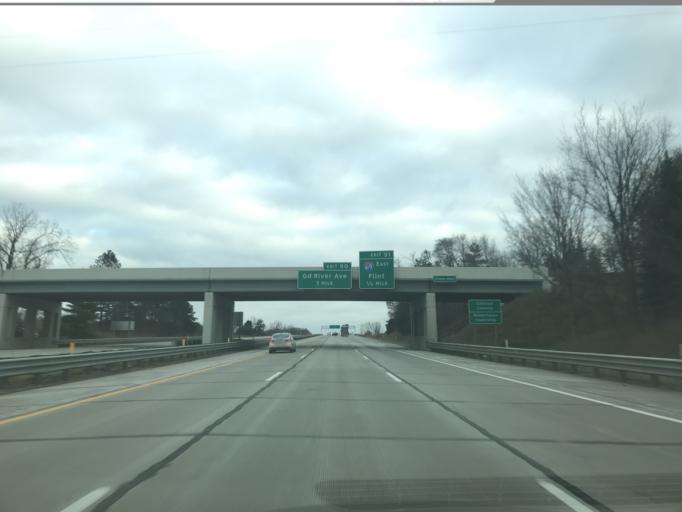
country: US
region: Michigan
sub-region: Eaton County
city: Waverly
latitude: 42.7692
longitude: -84.6687
